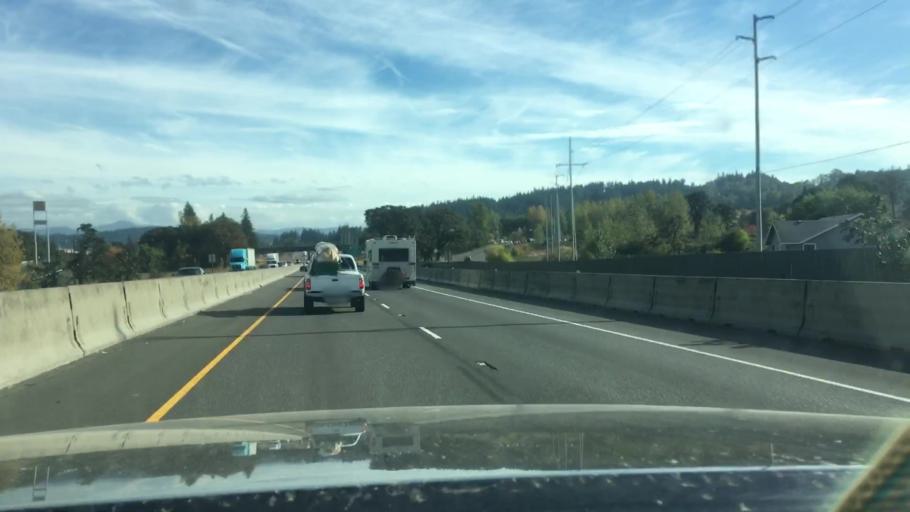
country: US
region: Oregon
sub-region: Lane County
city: Springfield
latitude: 44.0172
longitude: -123.0250
